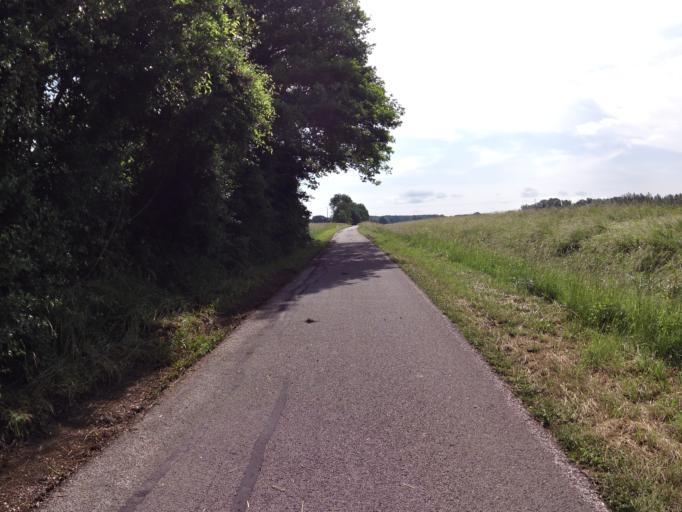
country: FR
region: Champagne-Ardenne
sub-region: Departement de l'Aube
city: Verrieres
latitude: 48.2647
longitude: 4.1797
